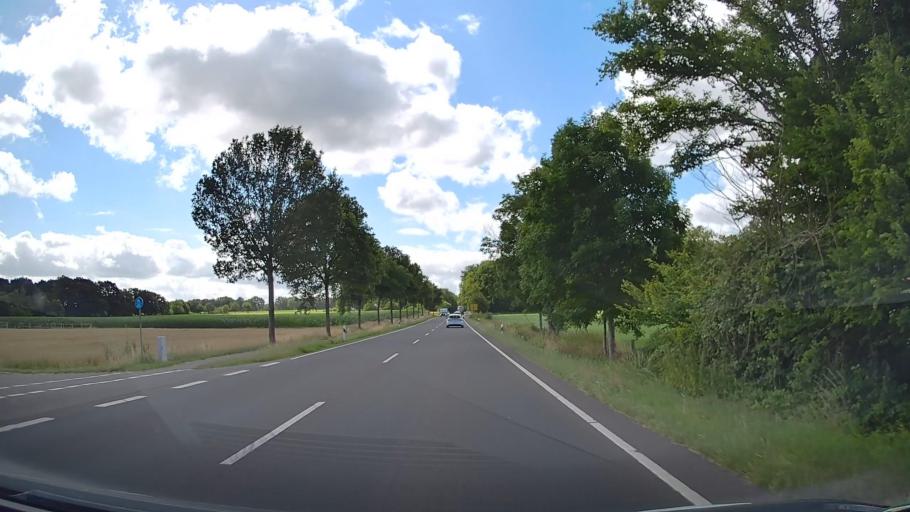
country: DE
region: Lower Saxony
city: Diepholz
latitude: 52.6631
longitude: 8.3306
